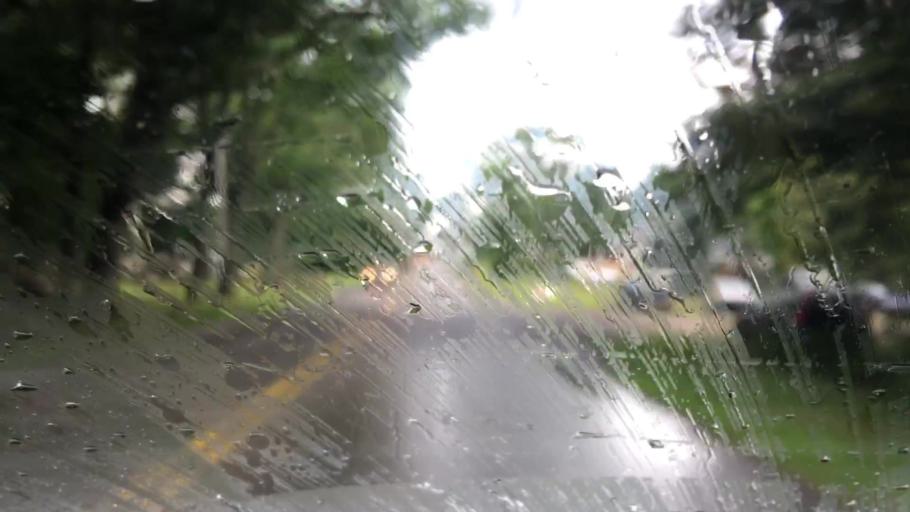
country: US
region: Maine
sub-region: York County
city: Wells Beach Station
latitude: 43.2963
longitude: -70.6028
